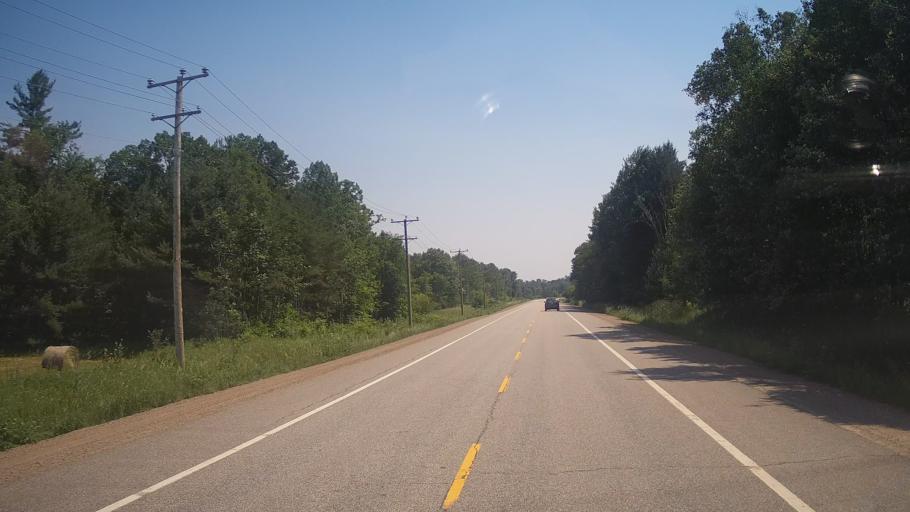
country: CA
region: Ontario
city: Pembroke
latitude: 45.8884
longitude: -76.9482
